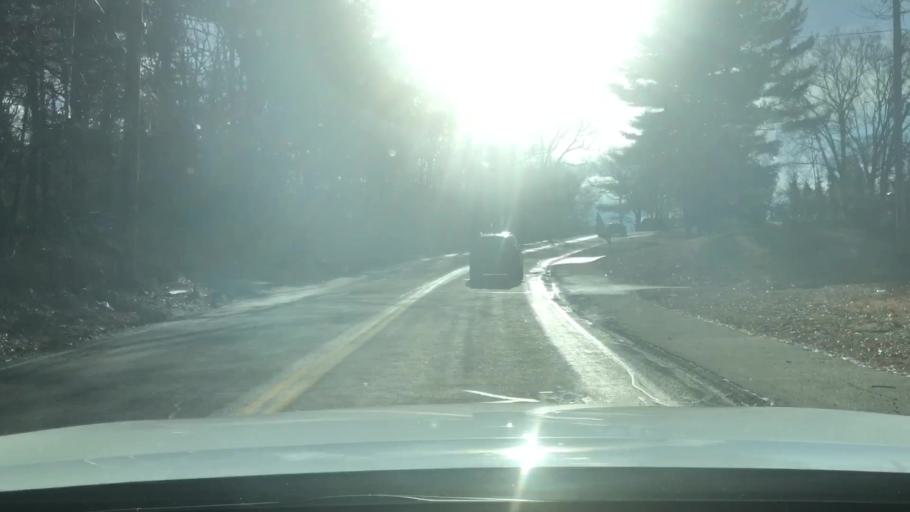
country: US
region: Rhode Island
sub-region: Providence County
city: Woonsocket
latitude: 42.0210
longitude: -71.4857
